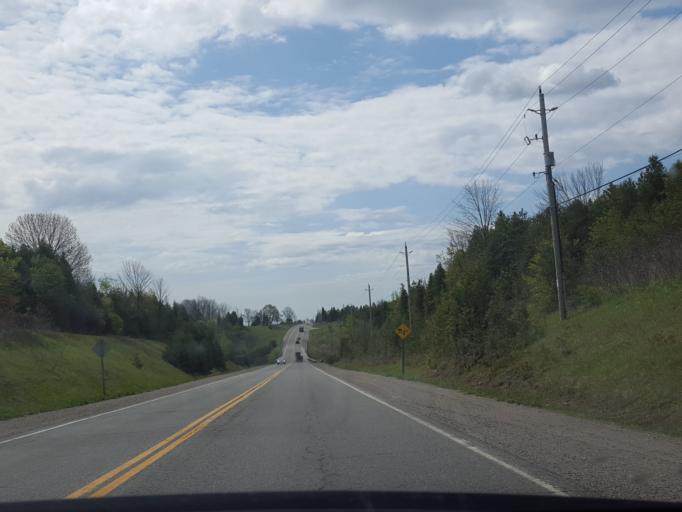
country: CA
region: Ontario
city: Oshawa
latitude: 43.9300
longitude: -78.7102
